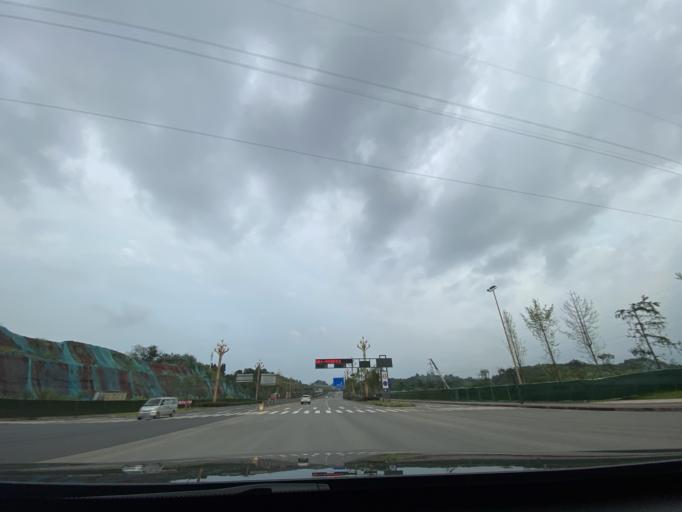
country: CN
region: Sichuan
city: Jiancheng
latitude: 30.4810
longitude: 104.4848
